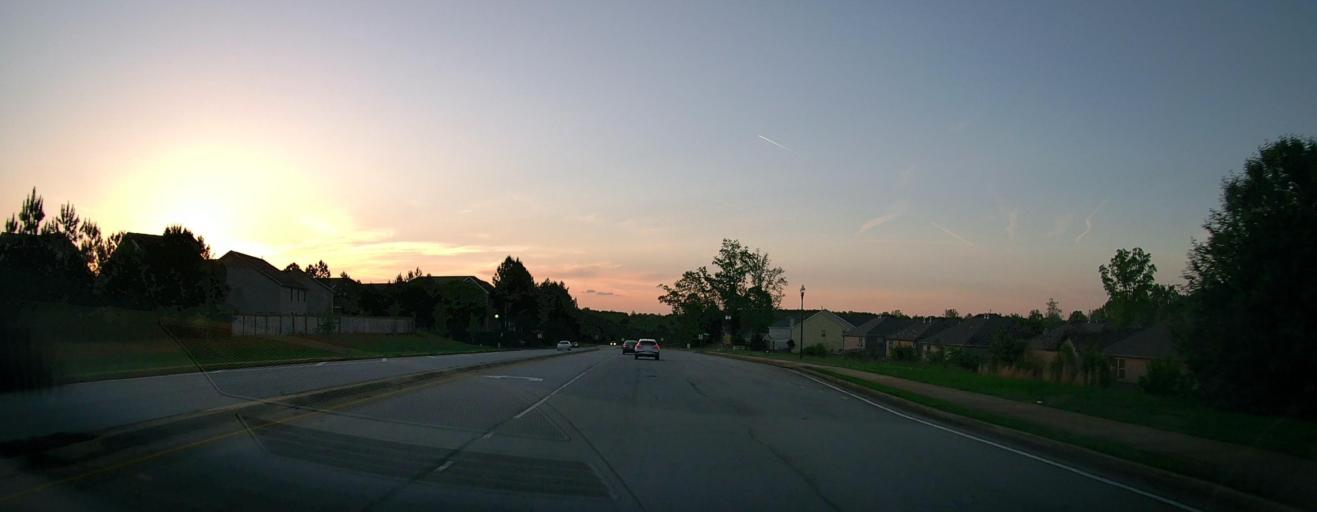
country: US
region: Georgia
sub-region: Henry County
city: McDonough
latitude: 33.4488
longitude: -84.1910
